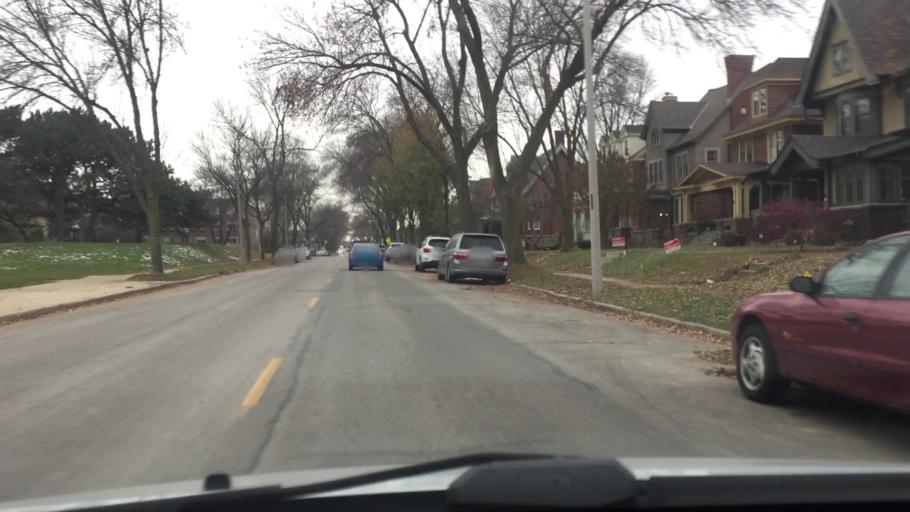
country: US
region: Wisconsin
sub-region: Milwaukee County
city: West Milwaukee
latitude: 43.0433
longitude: -87.9513
